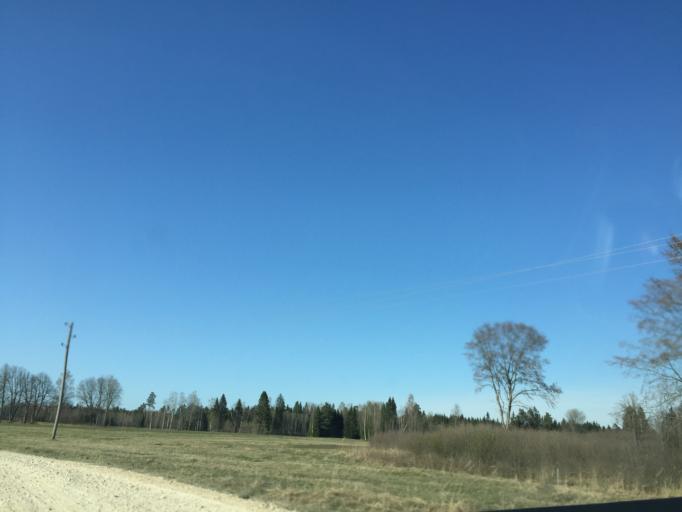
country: LV
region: Ropazu
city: Ropazi
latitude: 56.9412
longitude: 24.7058
